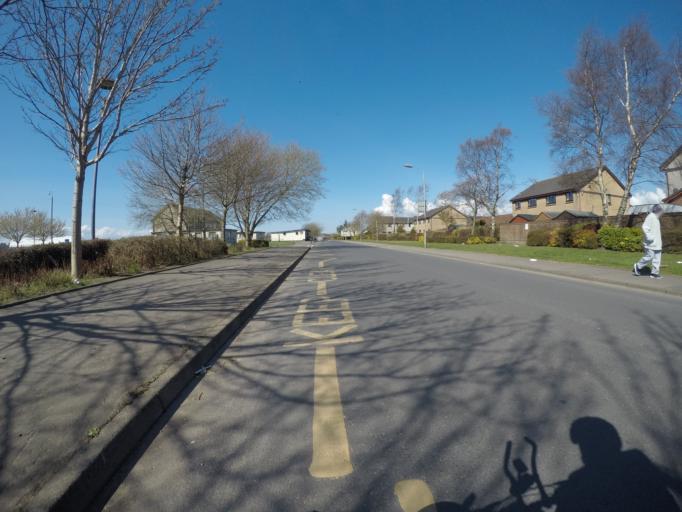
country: GB
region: Scotland
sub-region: North Ayrshire
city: Irvine
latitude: 55.6198
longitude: -4.6591
